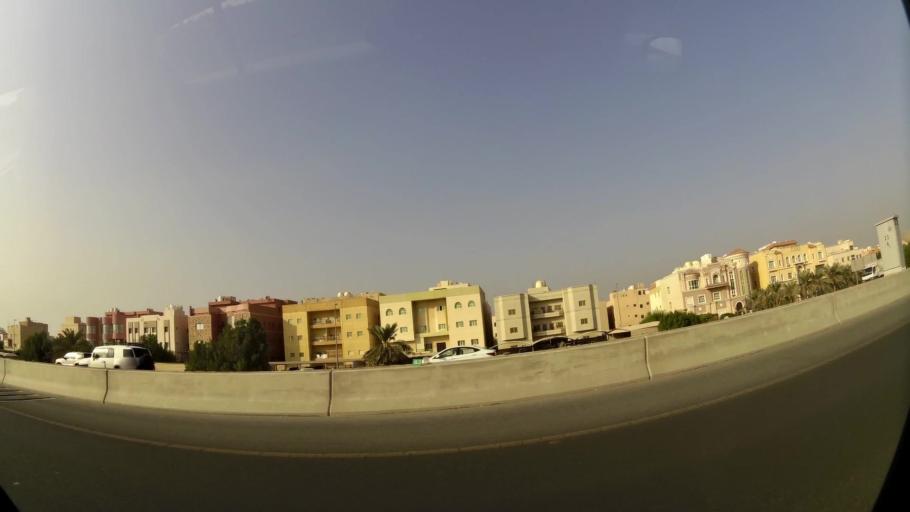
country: KW
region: Al Asimah
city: Ar Rabiyah
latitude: 29.2977
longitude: 47.8957
